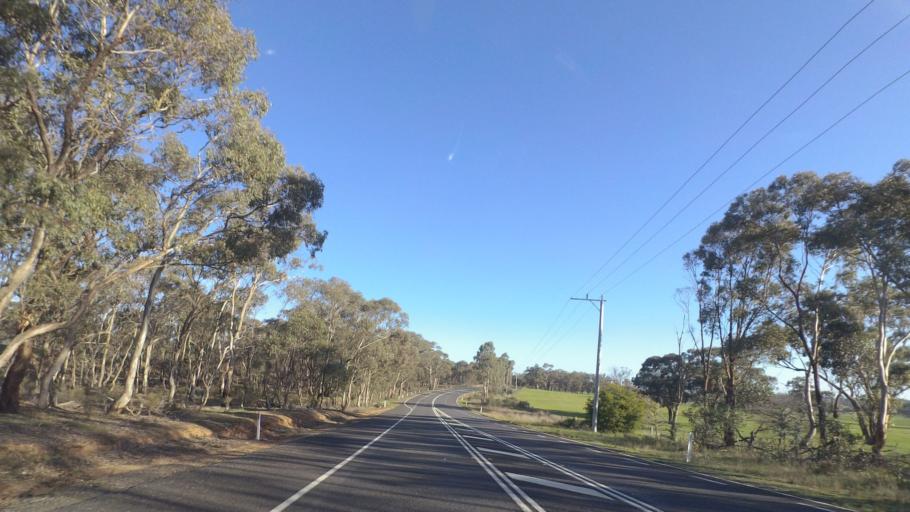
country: AU
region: Victoria
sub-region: Greater Bendigo
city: Kennington
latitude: -36.8575
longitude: 144.5056
